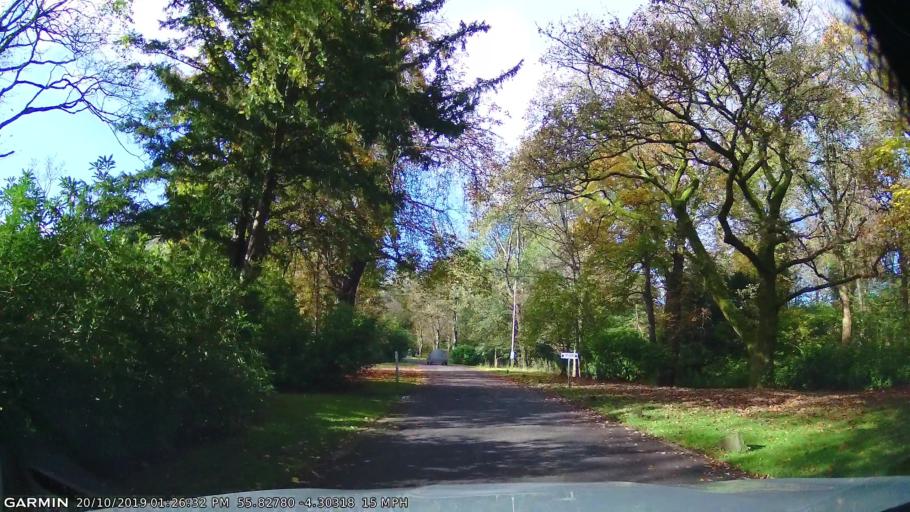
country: GB
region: Scotland
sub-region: East Renfrewshire
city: Giffnock
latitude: 55.8278
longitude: -4.3032
